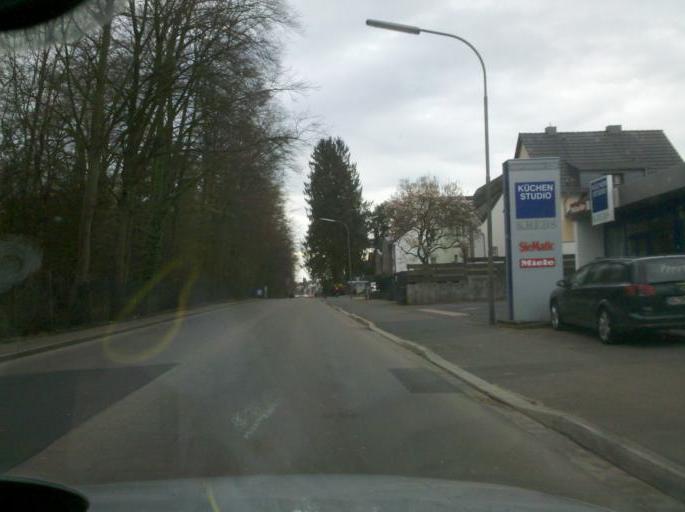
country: DE
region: North Rhine-Westphalia
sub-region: Regierungsbezirk Koln
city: Rosrath
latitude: 50.9058
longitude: 7.1861
